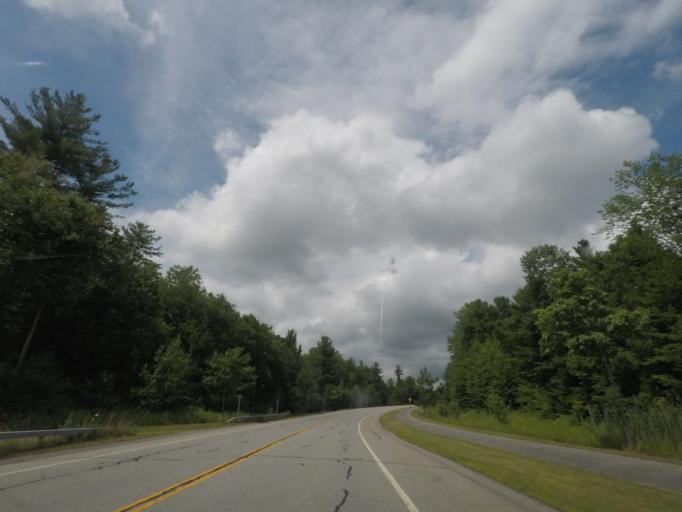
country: US
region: New York
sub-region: Saratoga County
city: Country Knolls
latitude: 42.9560
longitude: -73.7766
